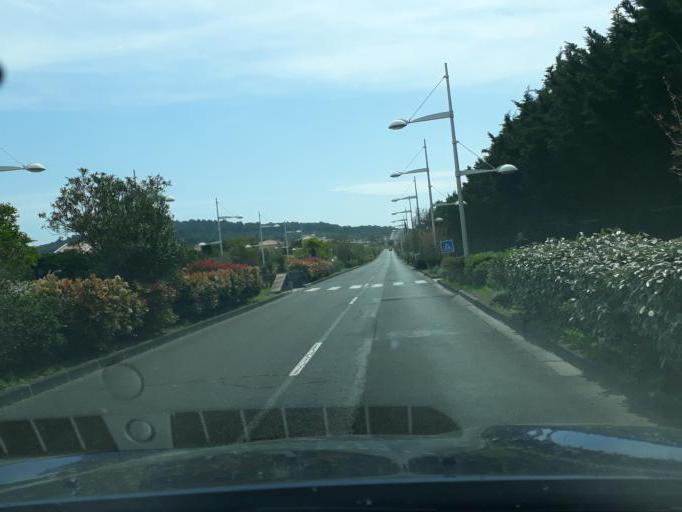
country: FR
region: Languedoc-Roussillon
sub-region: Departement de l'Herault
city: Agde
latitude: 43.3023
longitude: 3.4871
